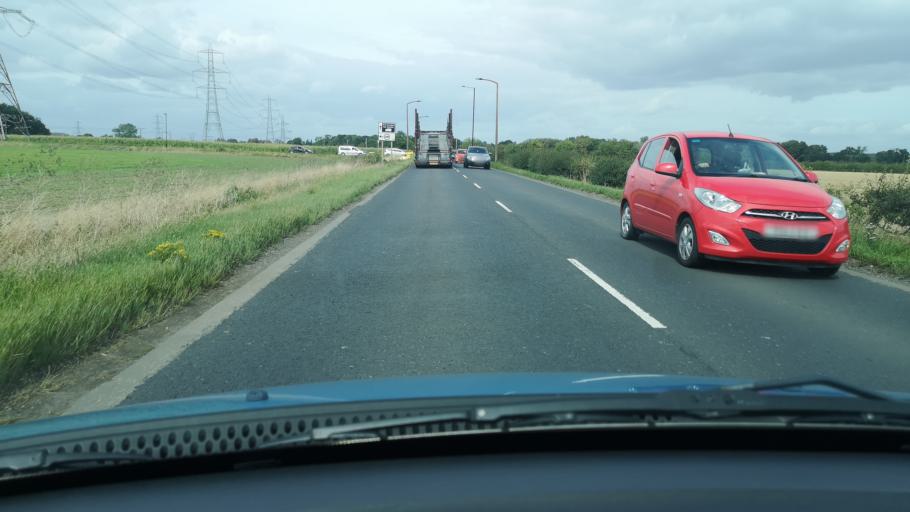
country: GB
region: England
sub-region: Doncaster
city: Kirk Sandall
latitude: 53.5610
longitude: -1.0561
